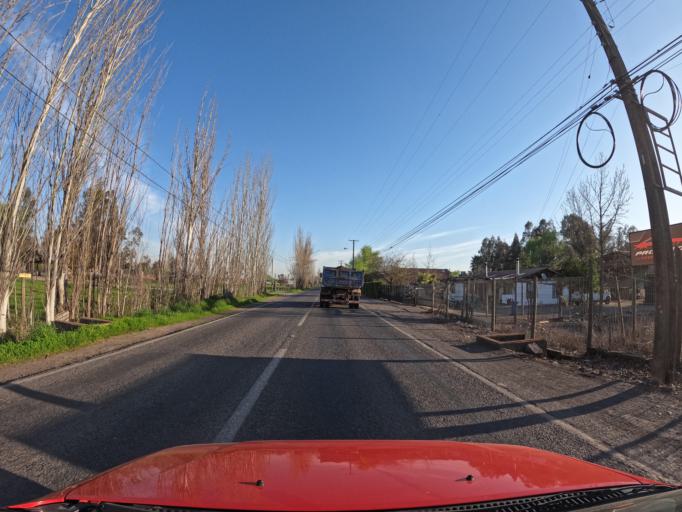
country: CL
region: Maule
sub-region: Provincia de Curico
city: Rauco
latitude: -34.8838
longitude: -71.2712
